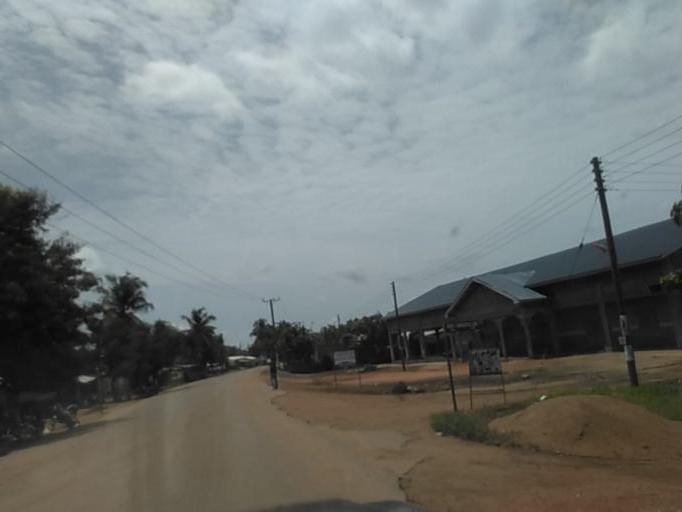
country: GH
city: Akropong
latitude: 6.0909
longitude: 0.1925
